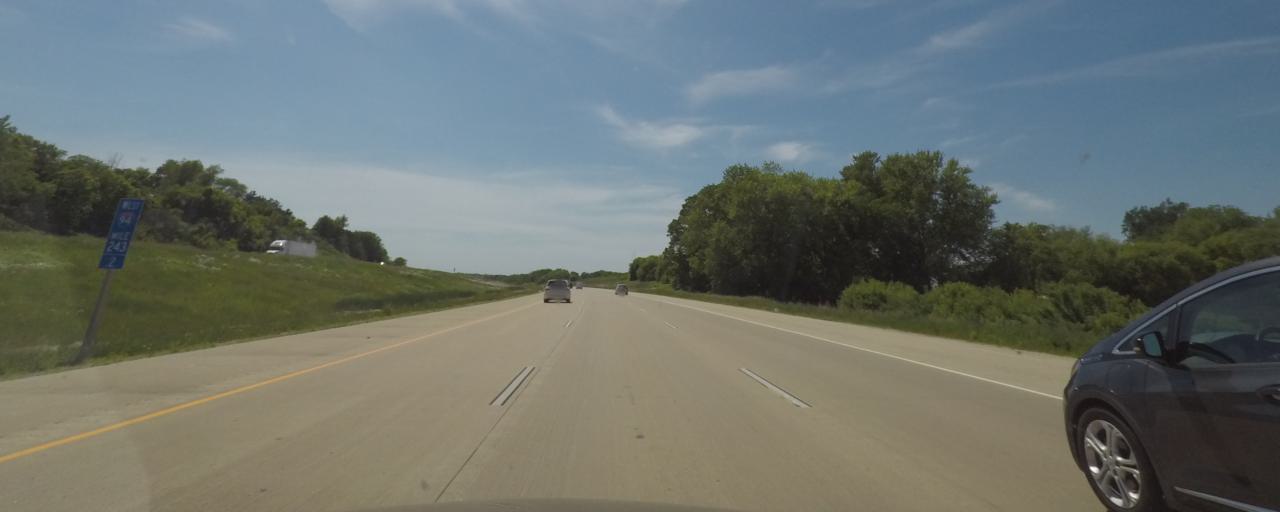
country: US
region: Wisconsin
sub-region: Dane County
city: Cottage Grove
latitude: 43.1085
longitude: -89.2272
